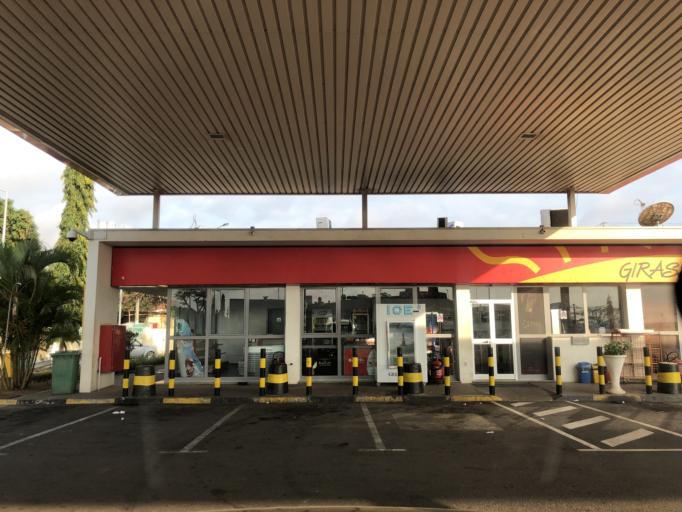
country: AO
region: Luanda
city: Luanda
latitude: -8.8973
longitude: 13.2289
